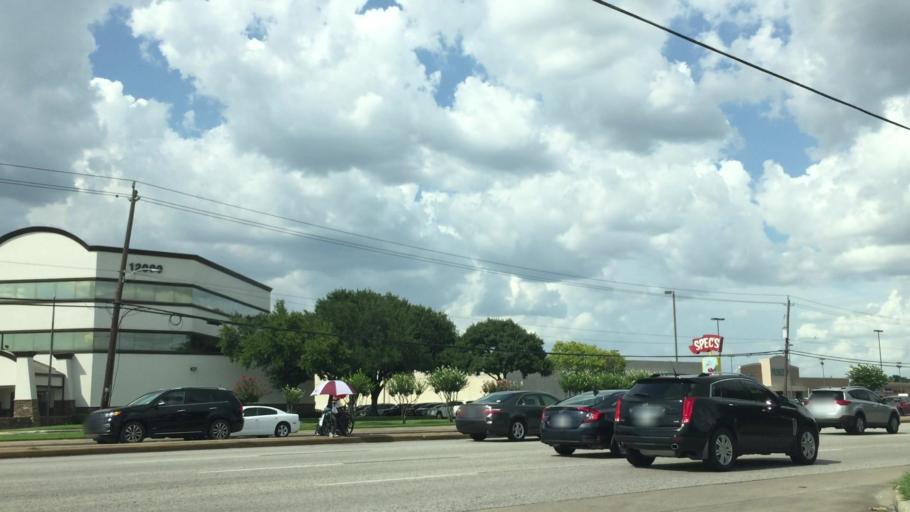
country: US
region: Texas
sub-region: Harris County
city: Bunker Hill Village
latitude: 29.7362
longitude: -95.5924
